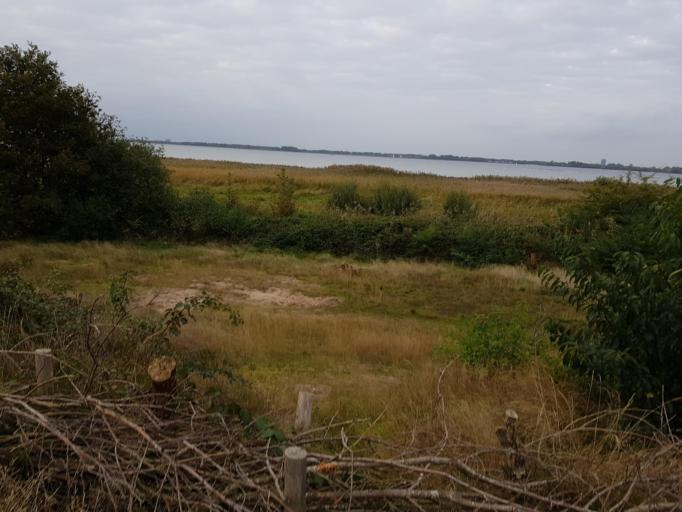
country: NL
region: North Holland
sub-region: Gemeente Huizen
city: Huizen
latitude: 52.3085
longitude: 5.2058
